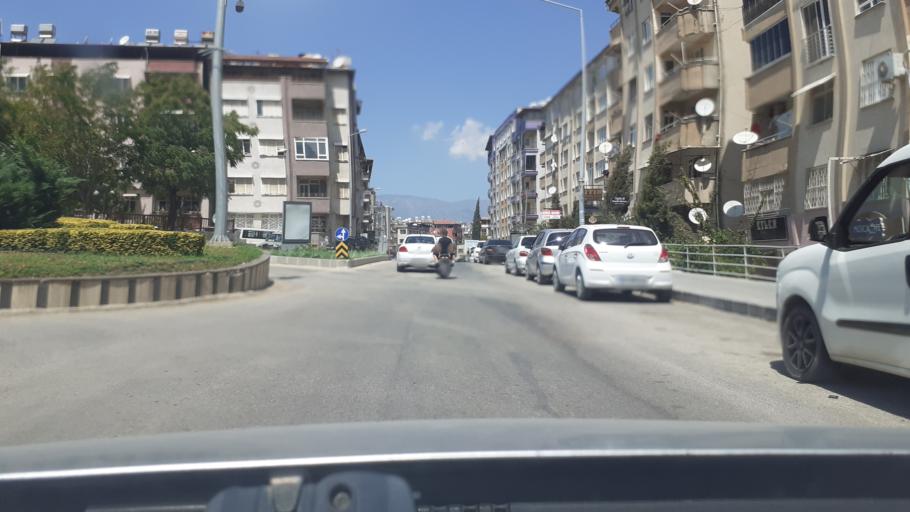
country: TR
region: Hatay
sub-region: Antakya Ilcesi
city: Antakya
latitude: 36.1964
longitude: 36.1555
